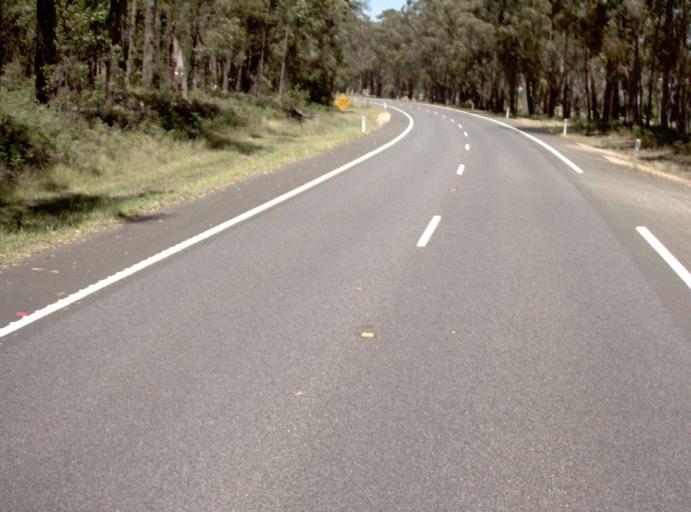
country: AU
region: Victoria
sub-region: East Gippsland
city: Lakes Entrance
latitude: -37.7773
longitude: 148.0504
